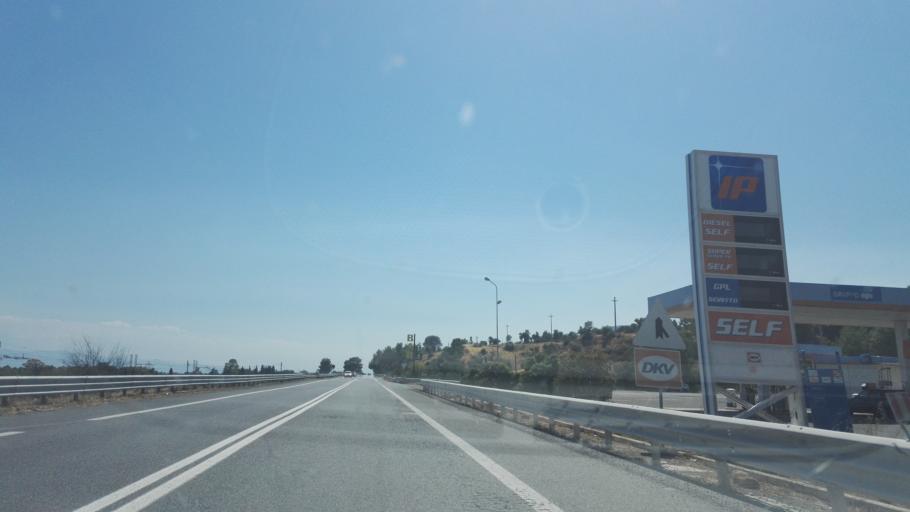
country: IT
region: Calabria
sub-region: Provincia di Cosenza
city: Marina
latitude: 39.9188
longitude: 16.5858
